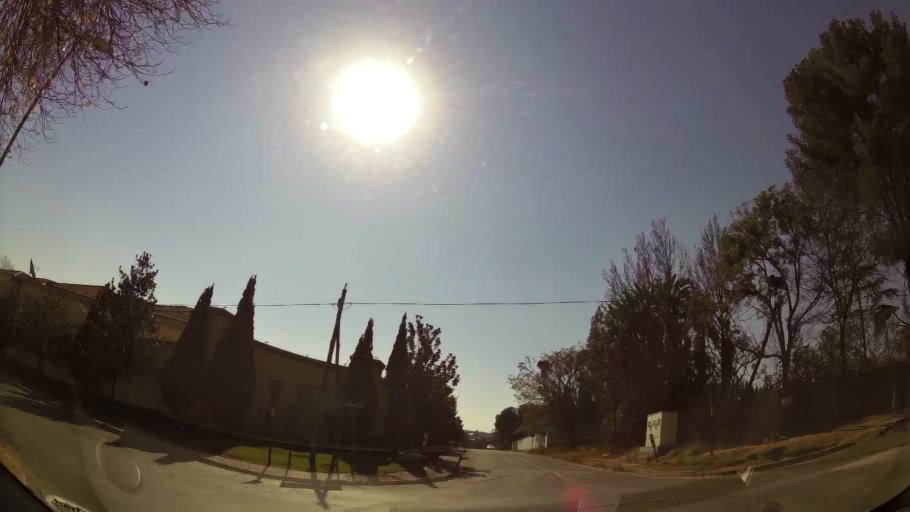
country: ZA
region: Gauteng
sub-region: City of Johannesburg Metropolitan Municipality
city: Johannesburg
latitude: -26.1082
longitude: 28.0432
